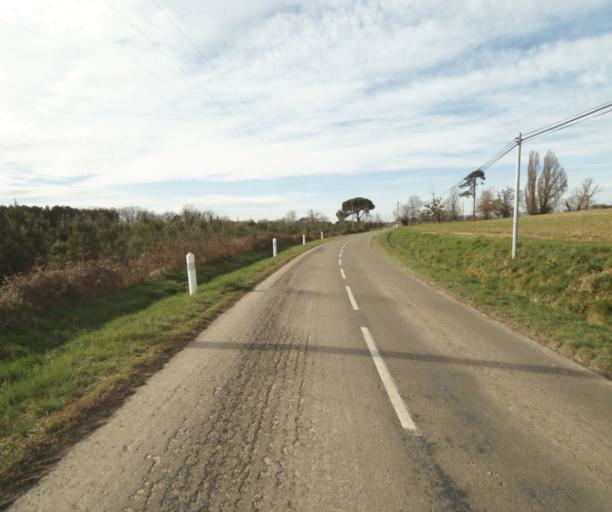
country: FR
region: Aquitaine
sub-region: Departement des Landes
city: Gabarret
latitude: 43.9800
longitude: 0.0341
